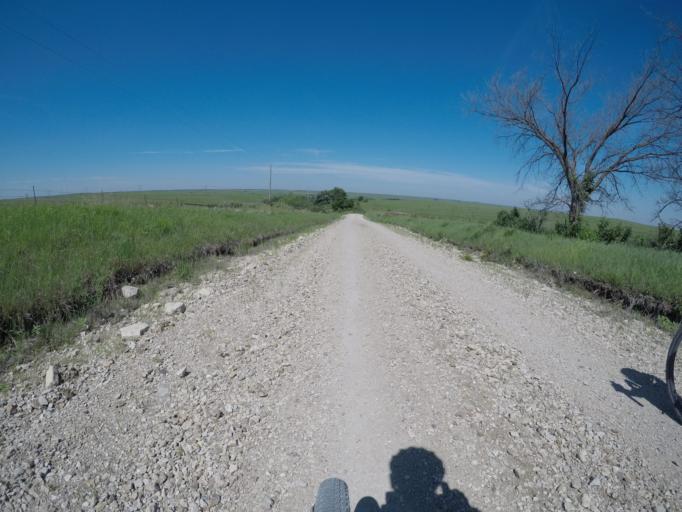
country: US
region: Kansas
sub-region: Wabaunsee County
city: Alma
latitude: 39.0007
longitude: -96.1825
